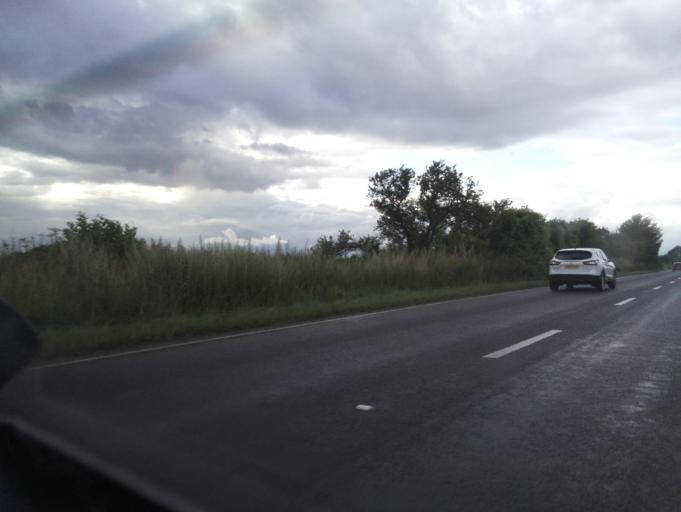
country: GB
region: England
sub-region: Oxfordshire
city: Woodstock
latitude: 51.8848
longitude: -1.3282
